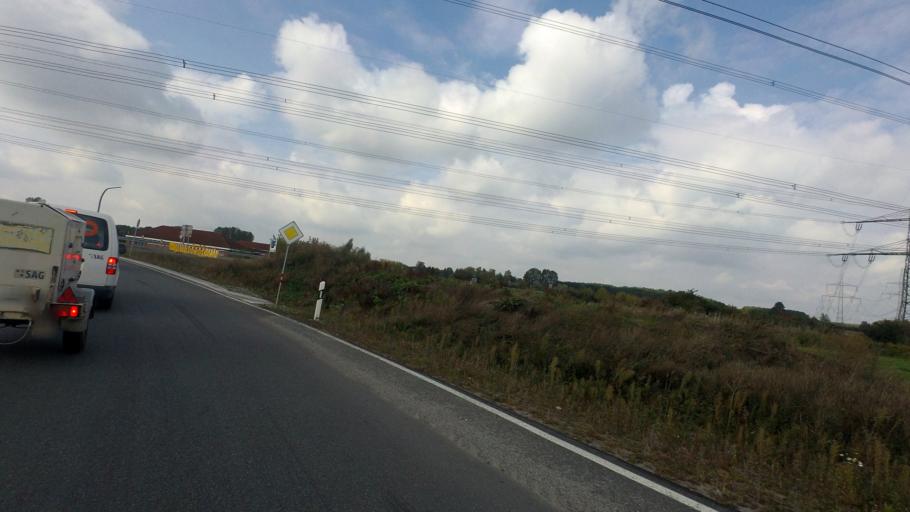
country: DE
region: Brandenburg
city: Bad Liebenwerda
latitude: 51.5143
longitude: 13.4287
